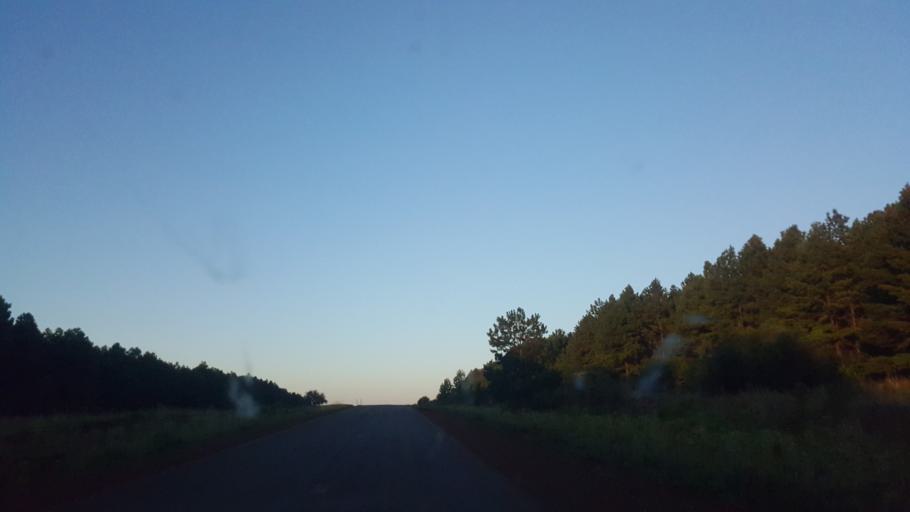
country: AR
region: Corrientes
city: Santo Tome
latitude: -28.4217
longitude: -55.9894
